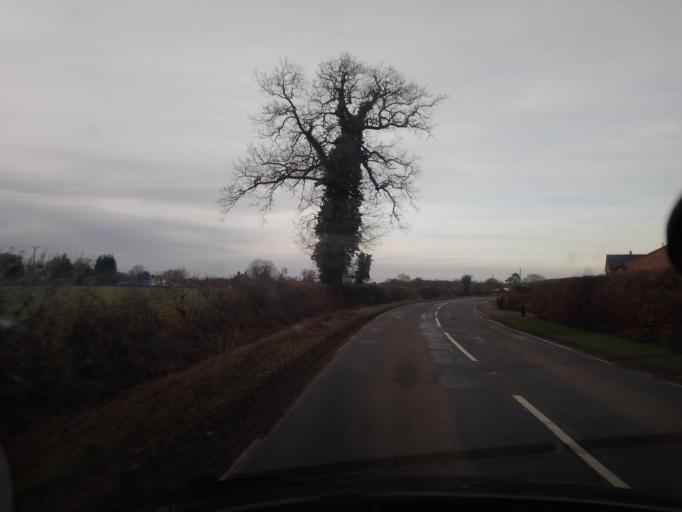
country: GB
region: England
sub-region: Shropshire
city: Prees
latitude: 52.9152
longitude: -2.6827
